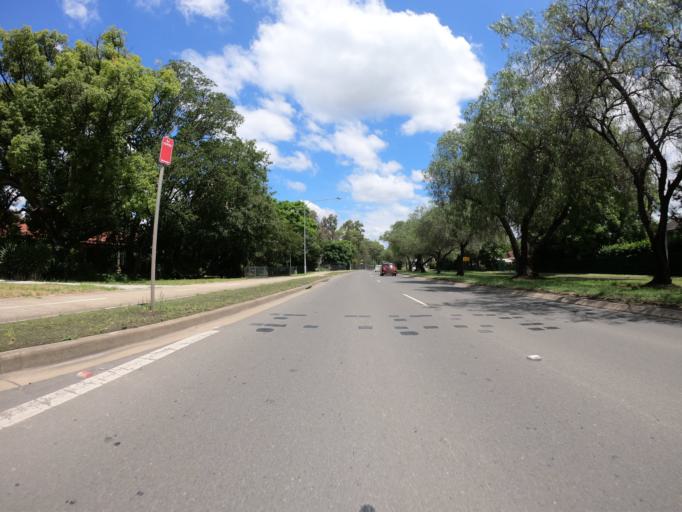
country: AU
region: New South Wales
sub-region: Penrith Municipality
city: Penrith
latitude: -33.7549
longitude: 150.6872
